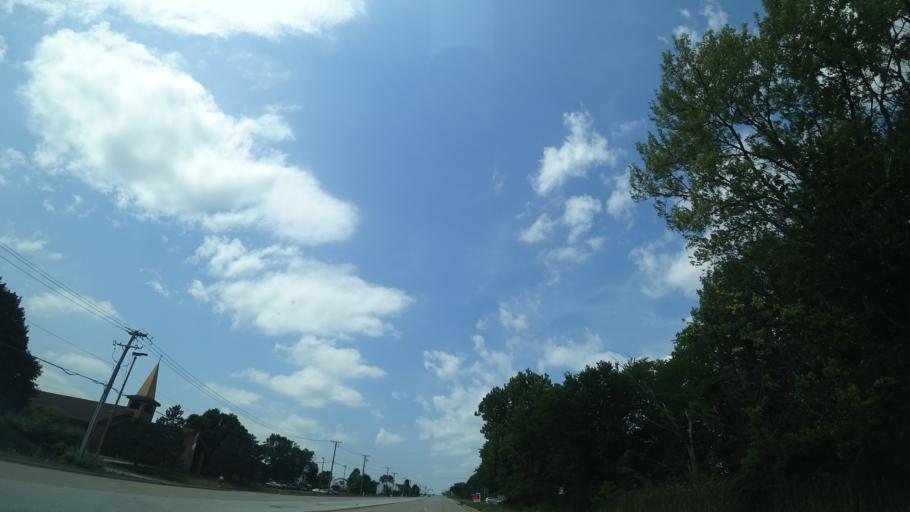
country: US
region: Illinois
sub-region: Will County
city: Frankfort Square
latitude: 41.5270
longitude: -87.7652
